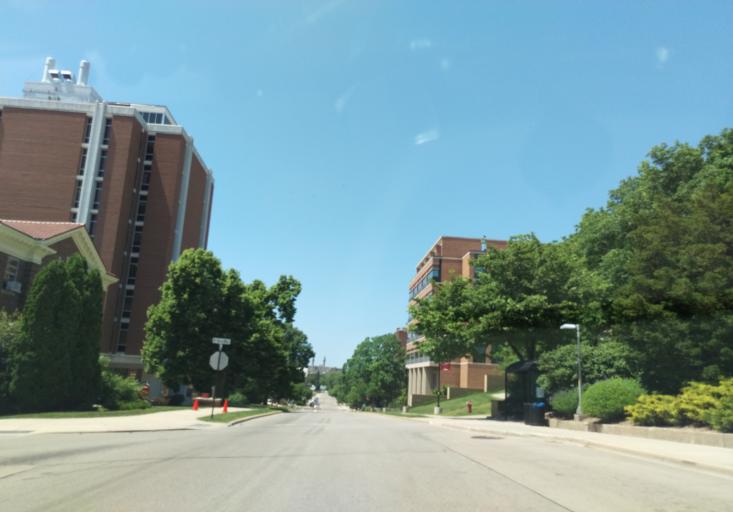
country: US
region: Wisconsin
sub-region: Dane County
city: Madison
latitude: 43.0752
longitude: -89.4102
